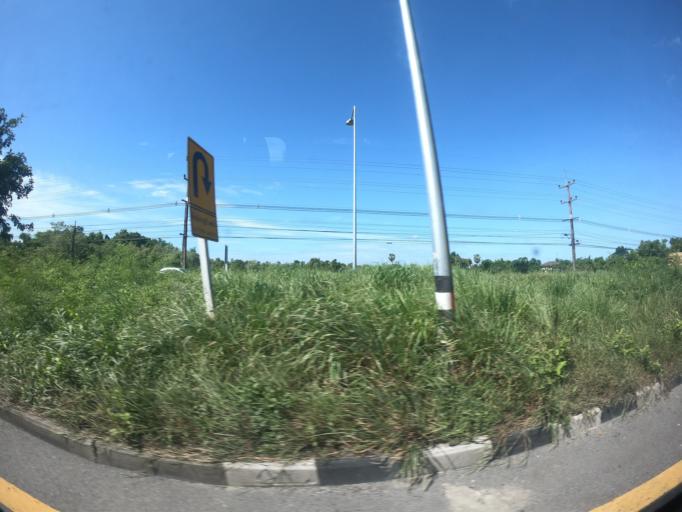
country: TH
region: Nakhon Nayok
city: Ban Na
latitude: 14.2425
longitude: 101.1165
